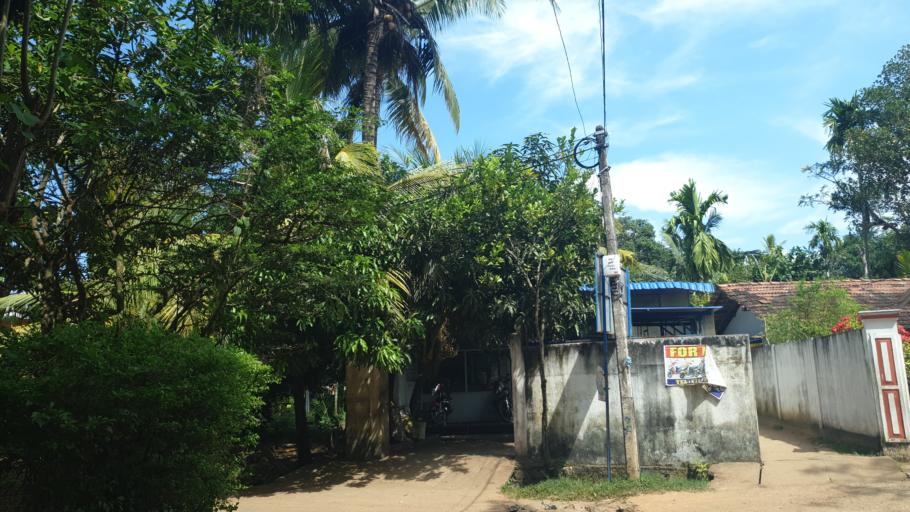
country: LK
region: Southern
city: Tangalla
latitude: 5.9646
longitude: 80.7094
